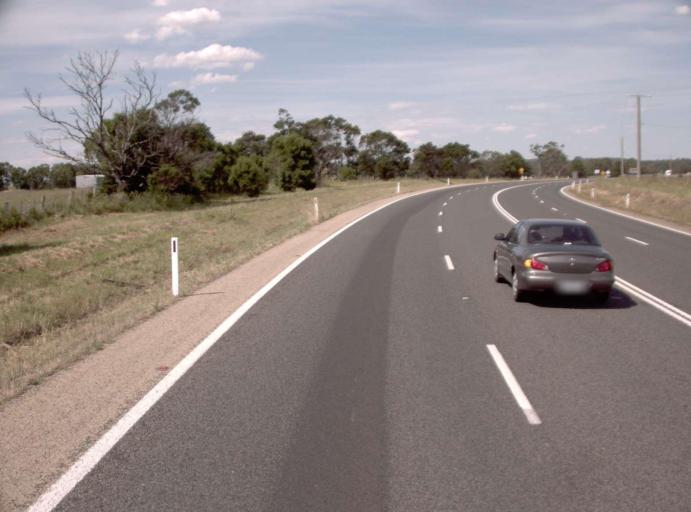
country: AU
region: Victoria
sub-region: East Gippsland
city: Bairnsdale
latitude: -37.8221
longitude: 147.7219
